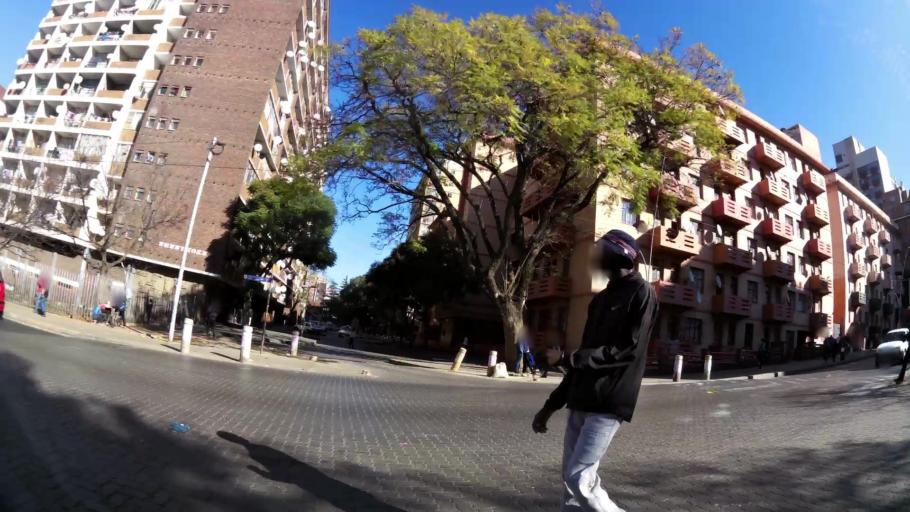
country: ZA
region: Gauteng
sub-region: City of Johannesburg Metropolitan Municipality
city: Johannesburg
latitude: -26.1921
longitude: 28.0495
